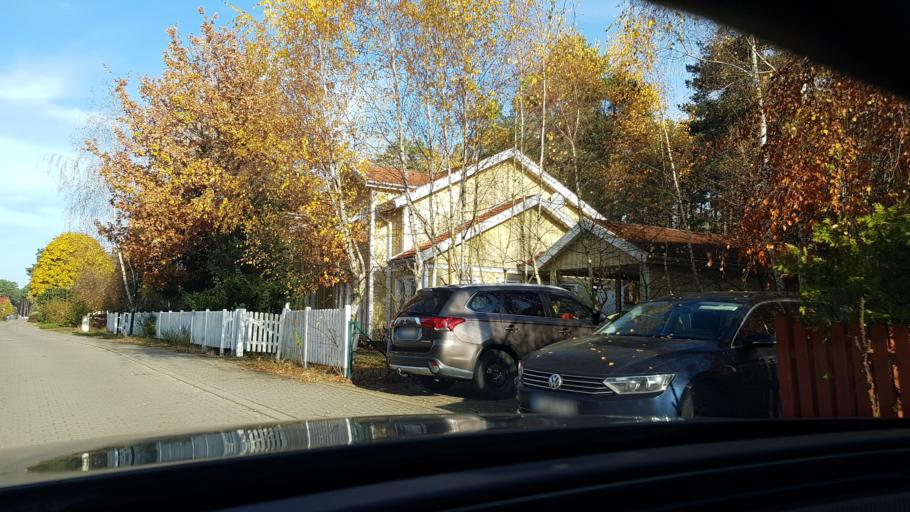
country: DE
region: Brandenburg
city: Borkwalde
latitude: 52.2554
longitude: 12.8425
